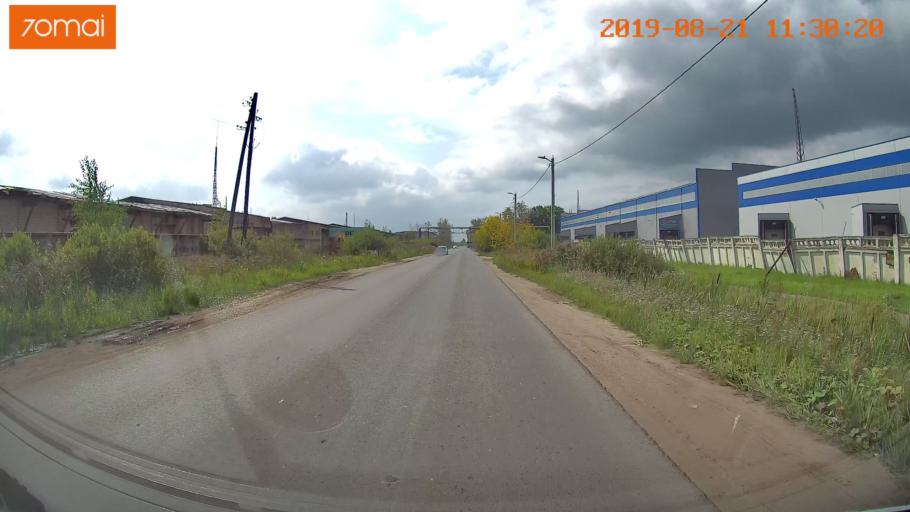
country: RU
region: Ivanovo
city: Novo-Talitsy
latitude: 56.9932
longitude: 40.9107
